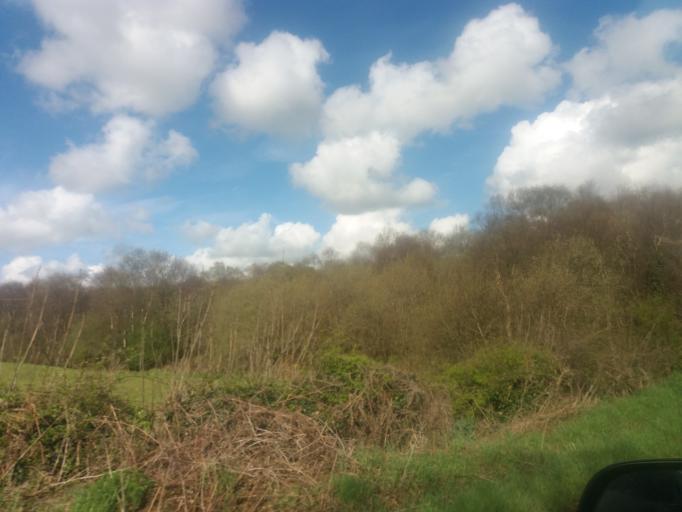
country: IE
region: Ulster
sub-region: An Cabhan
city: Virginia
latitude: 53.8416
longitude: -7.0938
